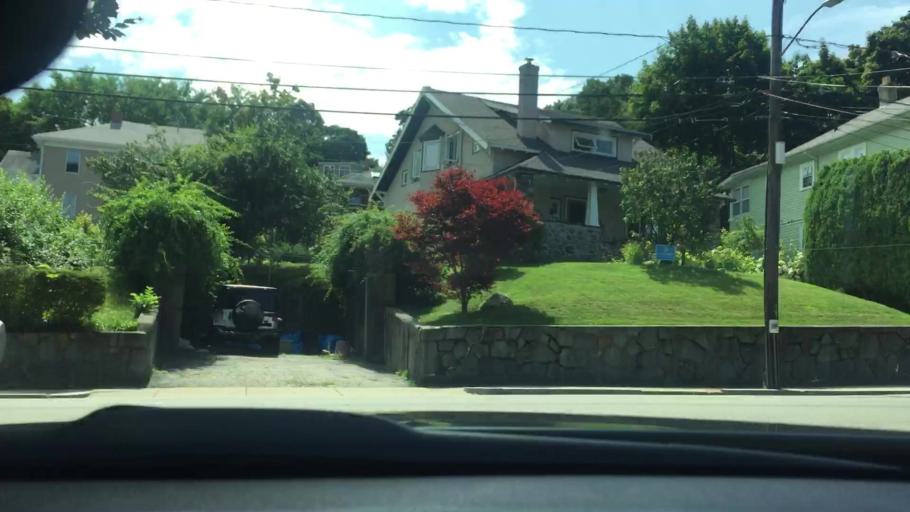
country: US
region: Massachusetts
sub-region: Middlesex County
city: Watertown
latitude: 42.3504
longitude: -71.1745
